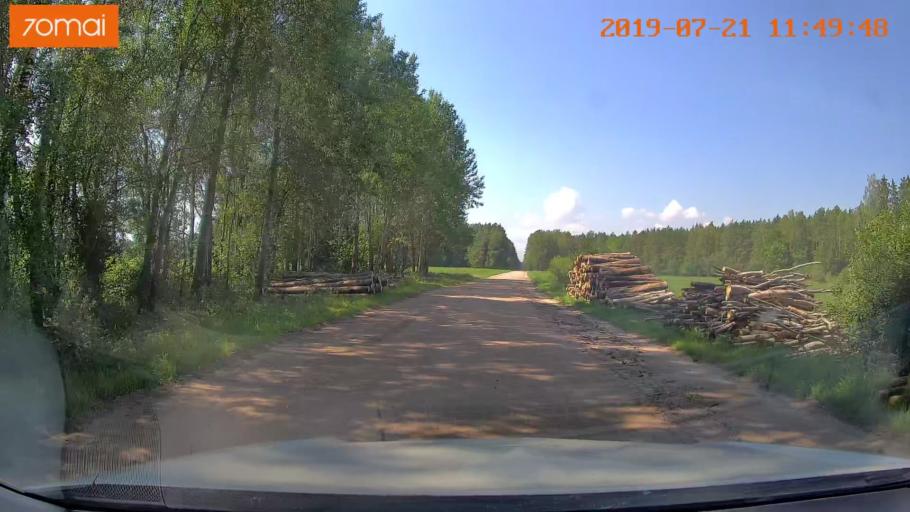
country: BY
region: Grodnenskaya
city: Lyubcha
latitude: 53.8905
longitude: 26.0347
